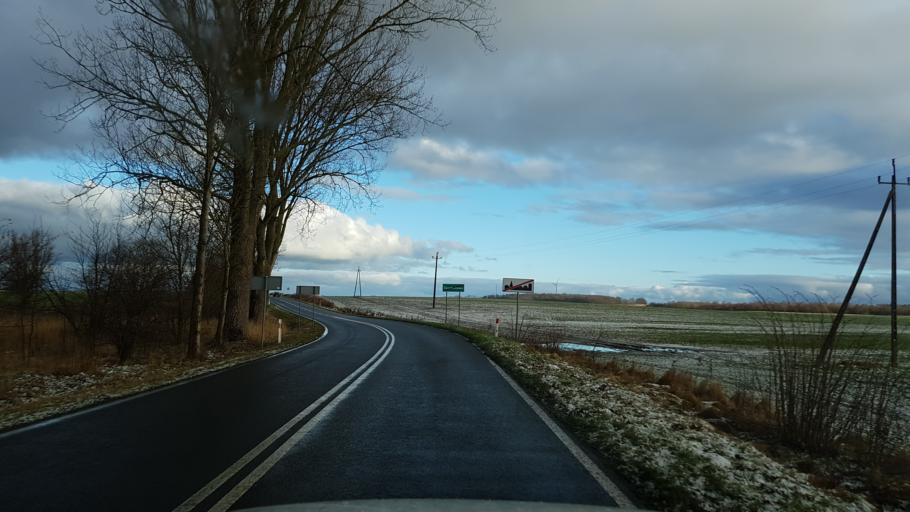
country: PL
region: West Pomeranian Voivodeship
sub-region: Powiat gryficki
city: Karnice
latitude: 54.0505
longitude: 15.0759
